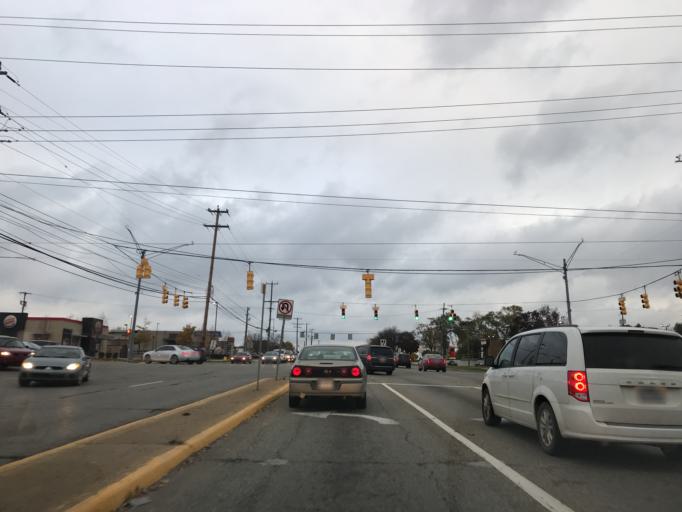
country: US
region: Michigan
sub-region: Oakland County
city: Farmington Hills
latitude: 42.4988
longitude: -83.3587
